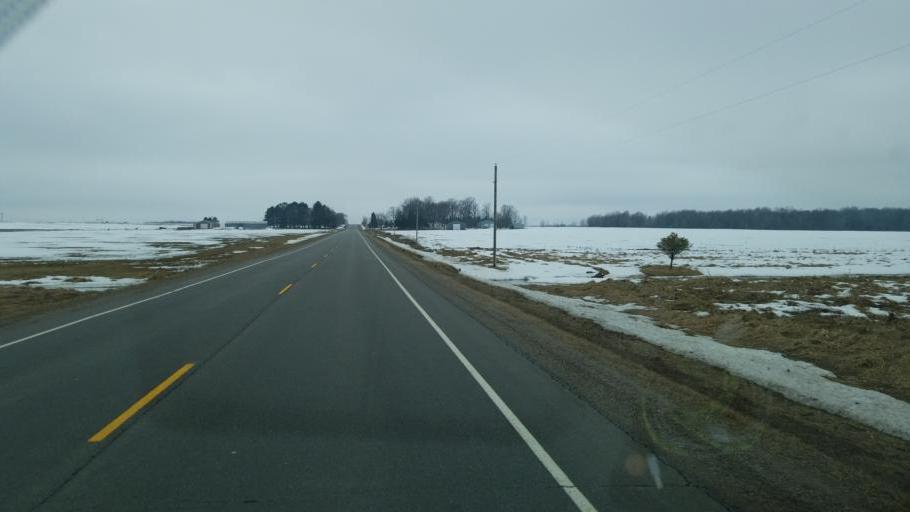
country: US
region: Wisconsin
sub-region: Marathon County
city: Spencer
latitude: 44.6561
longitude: -90.3184
